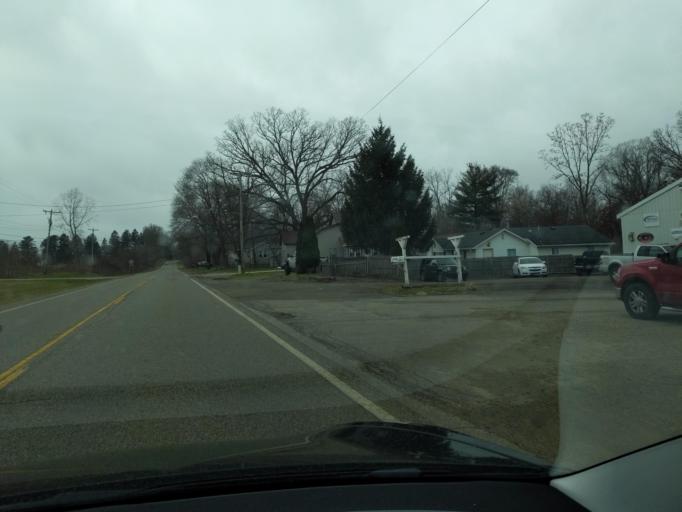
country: US
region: Michigan
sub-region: Jackson County
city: Spring Arbor
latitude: 42.2527
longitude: -84.5187
